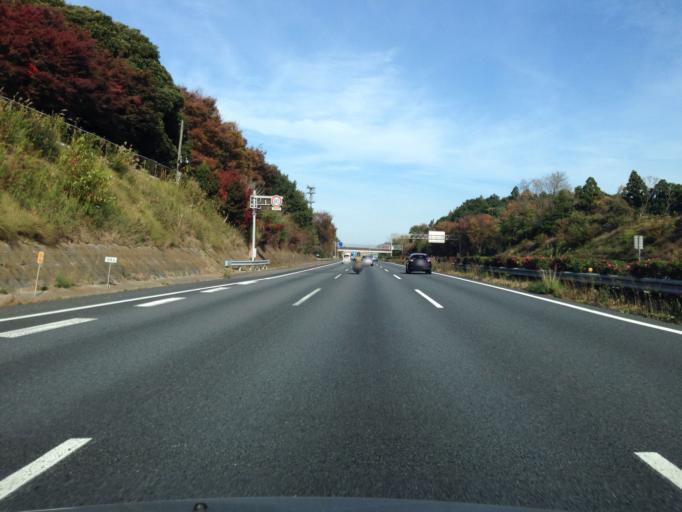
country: JP
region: Ibaraki
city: Ishioka
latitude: 36.1751
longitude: 140.2458
